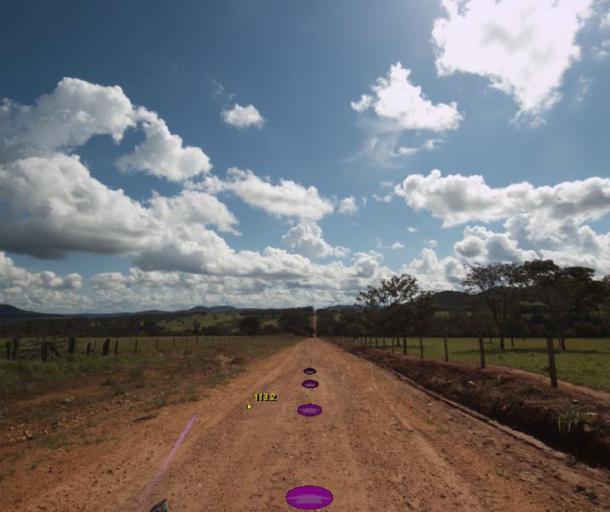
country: BR
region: Goias
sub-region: Pirenopolis
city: Pirenopolis
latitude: -15.8289
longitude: -49.1392
